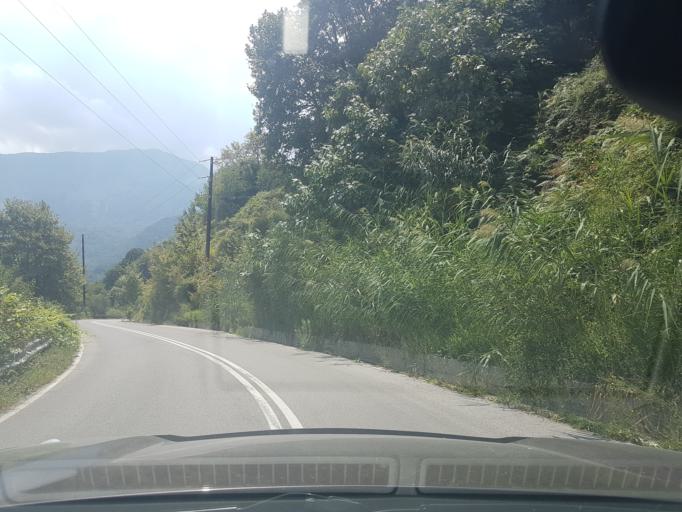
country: GR
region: Central Greece
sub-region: Nomos Evvoias
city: Kymi
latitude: 38.6369
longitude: 23.9448
